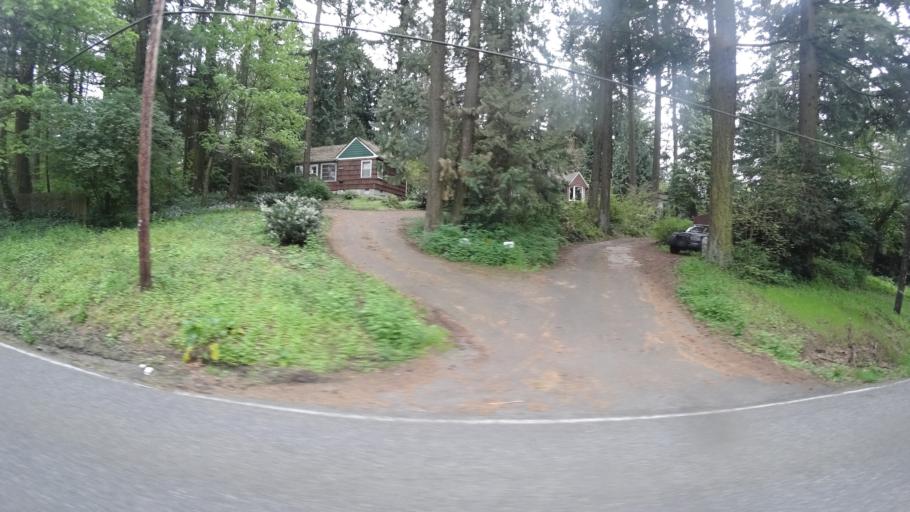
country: US
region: Oregon
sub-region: Washington County
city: Metzger
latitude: 45.4444
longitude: -122.7349
